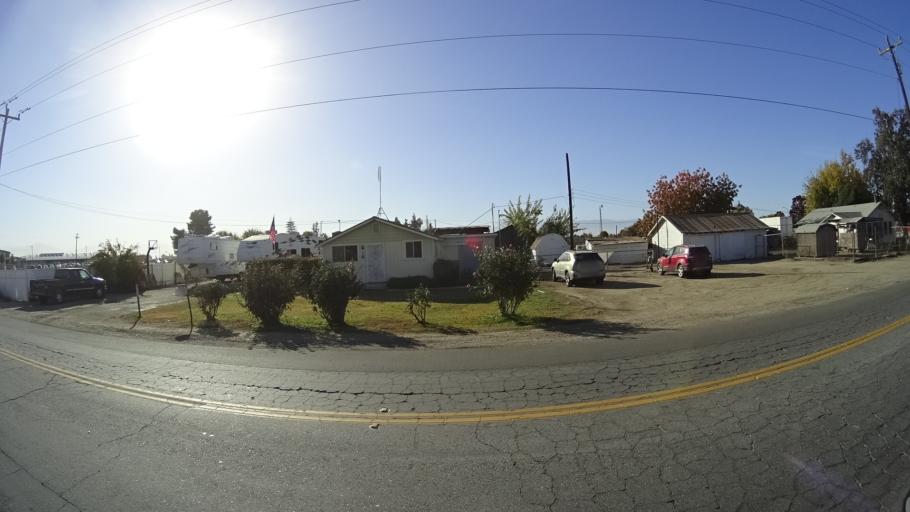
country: US
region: California
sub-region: Kern County
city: Greenfield
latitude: 35.2741
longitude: -119.0381
